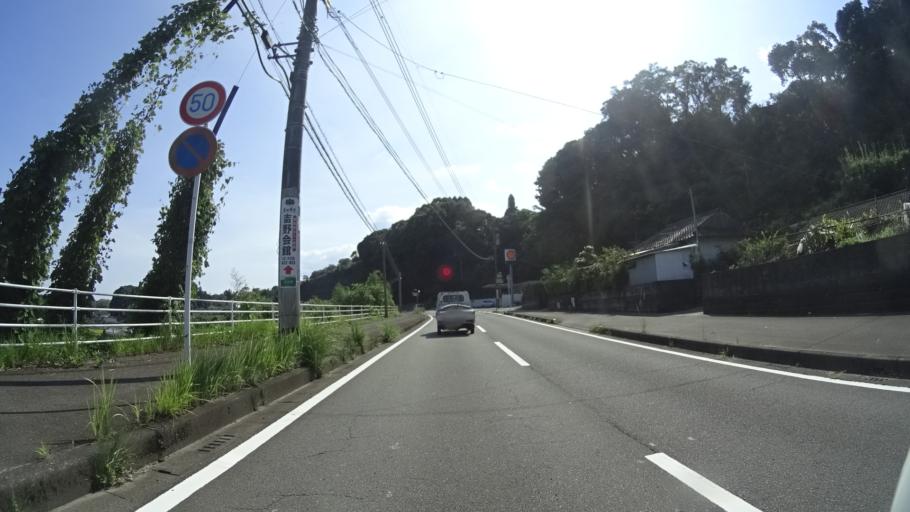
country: JP
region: Kagoshima
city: Kagoshima-shi
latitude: 31.6578
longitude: 130.5504
